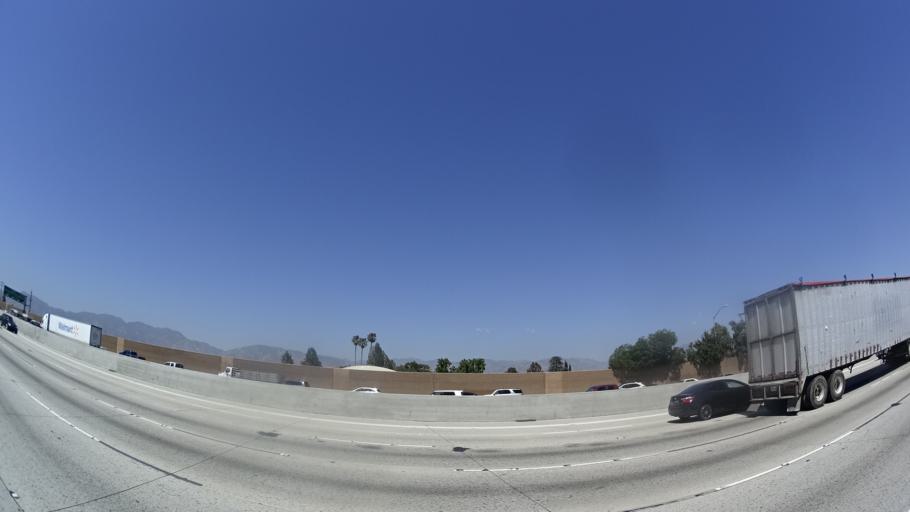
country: US
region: California
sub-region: Los Angeles County
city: San Fernando
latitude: 34.2479
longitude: -118.4261
